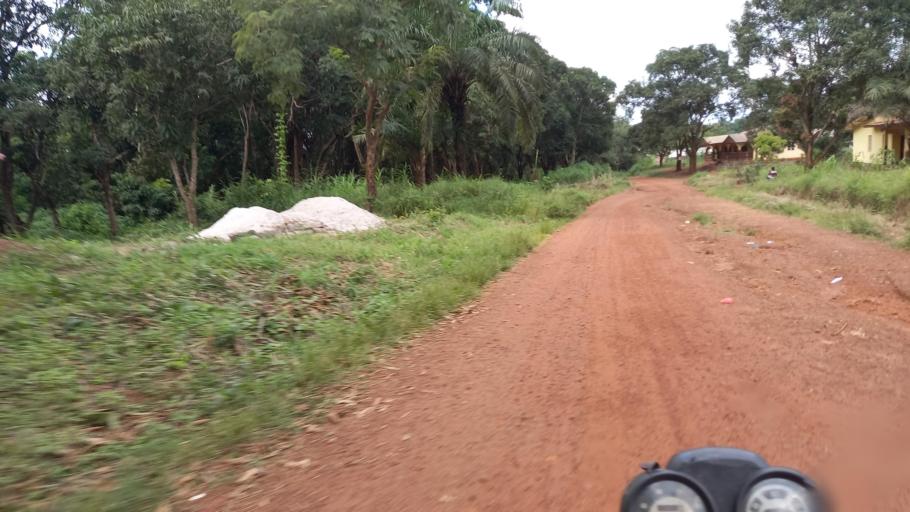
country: SL
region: Northern Province
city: Kamakwie
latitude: 9.5022
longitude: -12.2364
